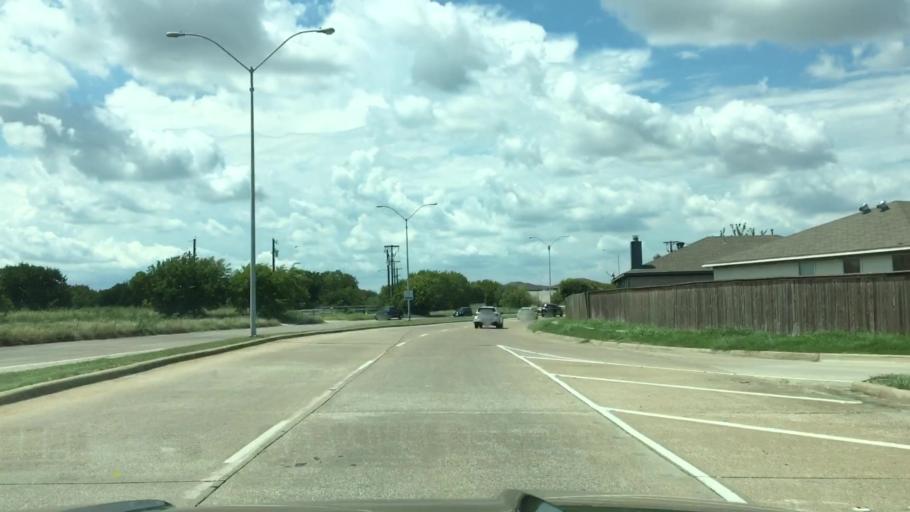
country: US
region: Texas
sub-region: Tarrant County
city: Blue Mound
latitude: 32.8614
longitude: -97.3332
